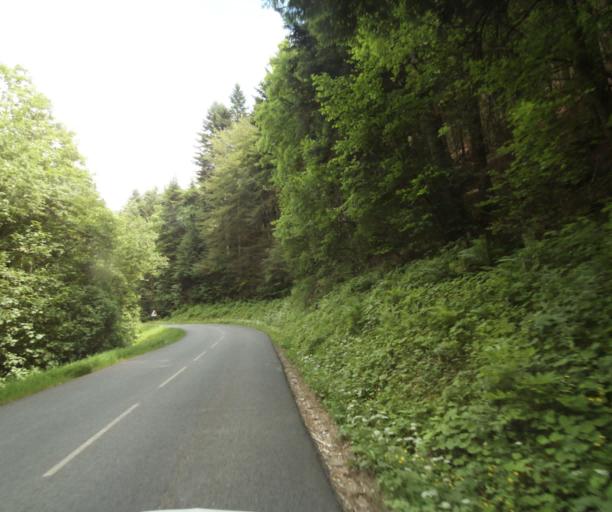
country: FR
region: Rhone-Alpes
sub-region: Departement de la Haute-Savoie
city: Perrignier
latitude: 46.2635
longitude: 6.4342
